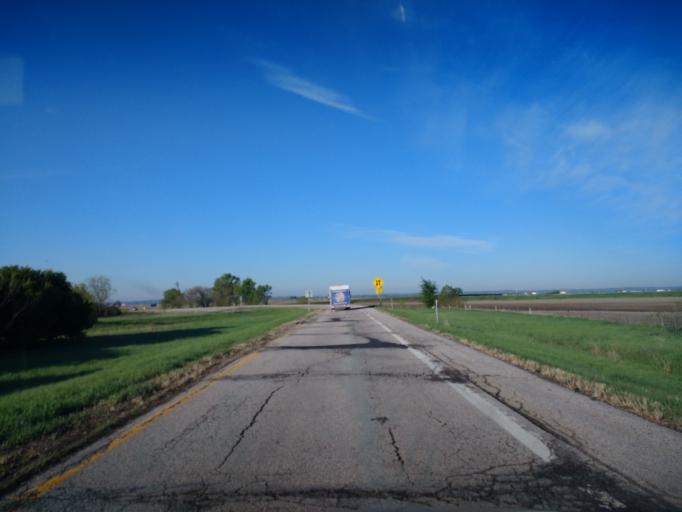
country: US
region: Iowa
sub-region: Harrison County
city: Missouri Valley
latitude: 41.5021
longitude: -95.9033
